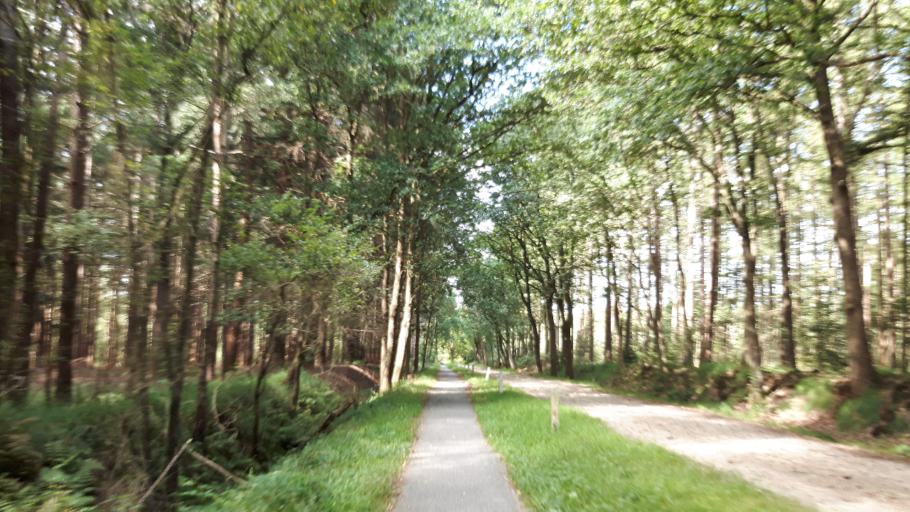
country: NL
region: Friesland
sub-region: Gemeente Smallingerland
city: Drachtstercompagnie
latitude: 53.0813
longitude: 6.2365
